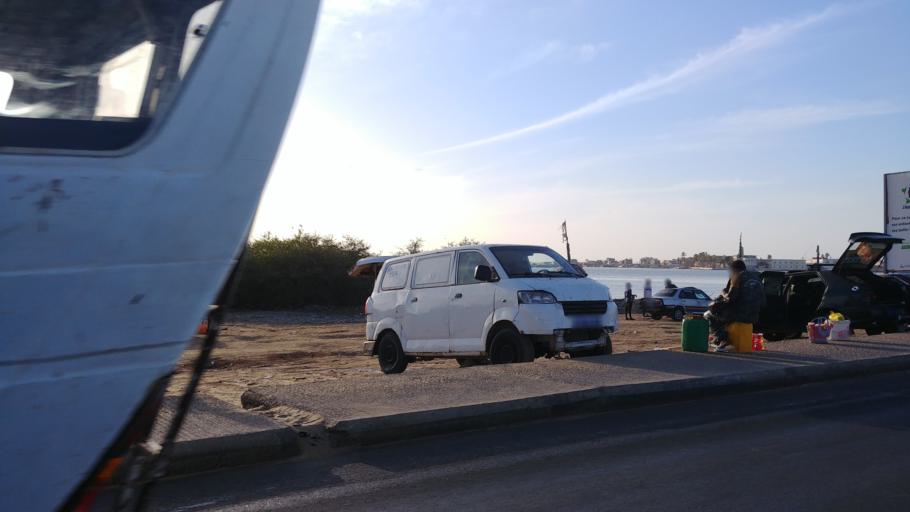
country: SN
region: Saint-Louis
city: Saint-Louis
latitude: 16.0154
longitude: -16.4990
